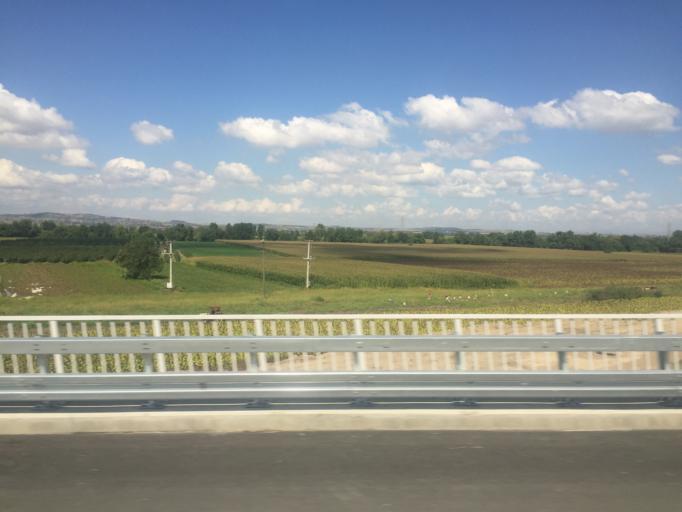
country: TR
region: Balikesir
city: Gobel
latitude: 40.0293
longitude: 28.2118
